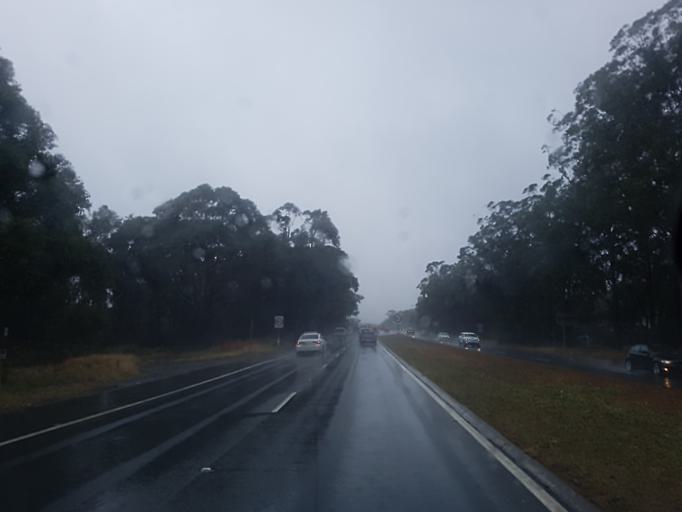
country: AU
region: New South Wales
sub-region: Warringah
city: Davidson
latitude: -33.7020
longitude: 151.2096
